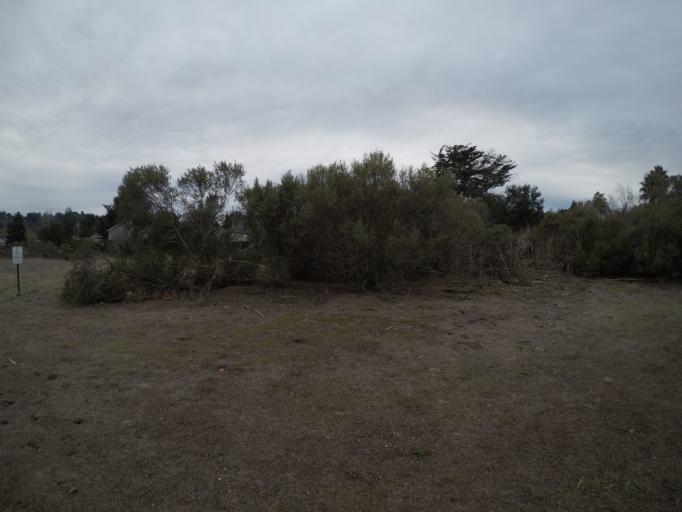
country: US
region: California
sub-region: Santa Cruz County
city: Scotts Valley
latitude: 37.0674
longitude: -122.0095
